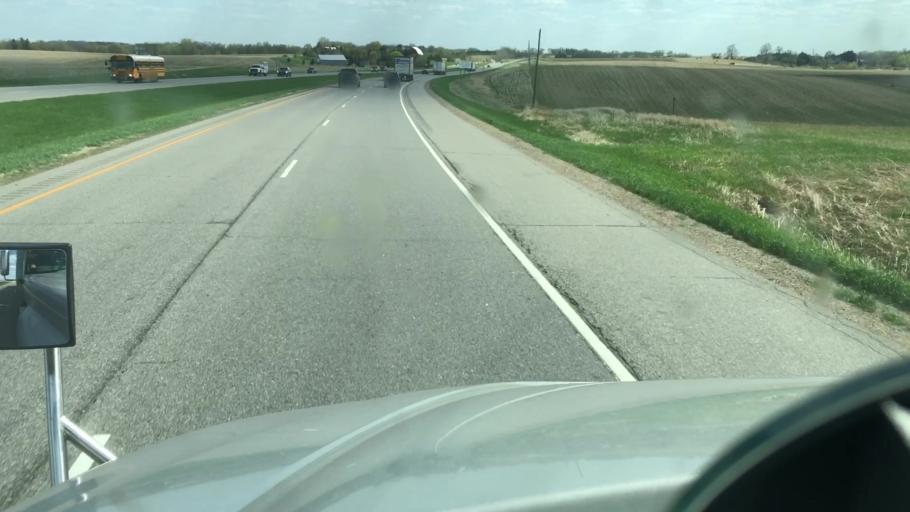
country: US
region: Minnesota
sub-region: Le Sueur County
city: Le Sueur
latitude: 44.5362
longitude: -93.8479
